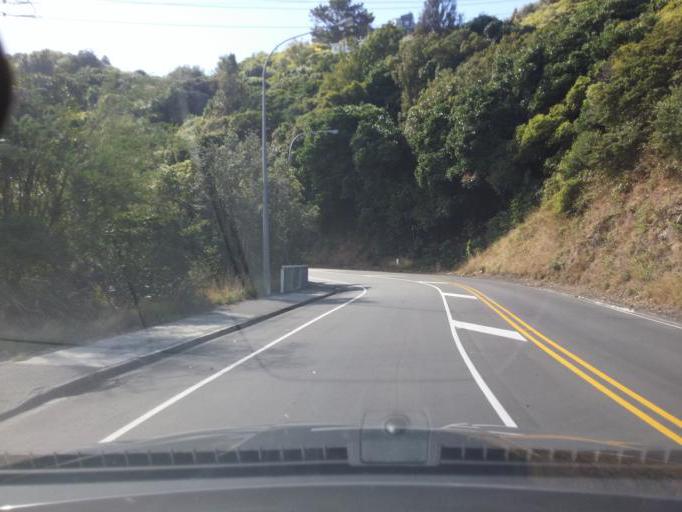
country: NZ
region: Wellington
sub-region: Wellington City
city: Kelburn
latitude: -41.2572
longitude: 174.7794
